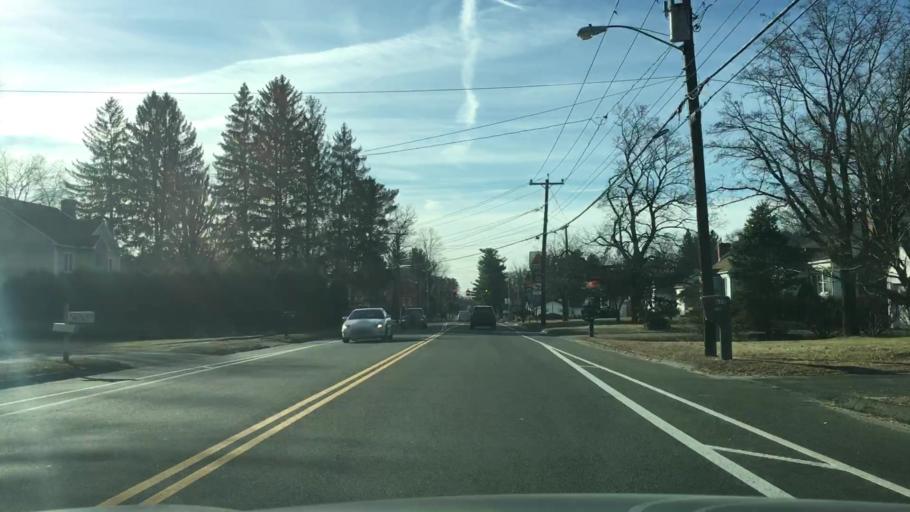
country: US
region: Massachusetts
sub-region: Hampden County
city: Agawam
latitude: 42.0687
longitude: -72.6314
